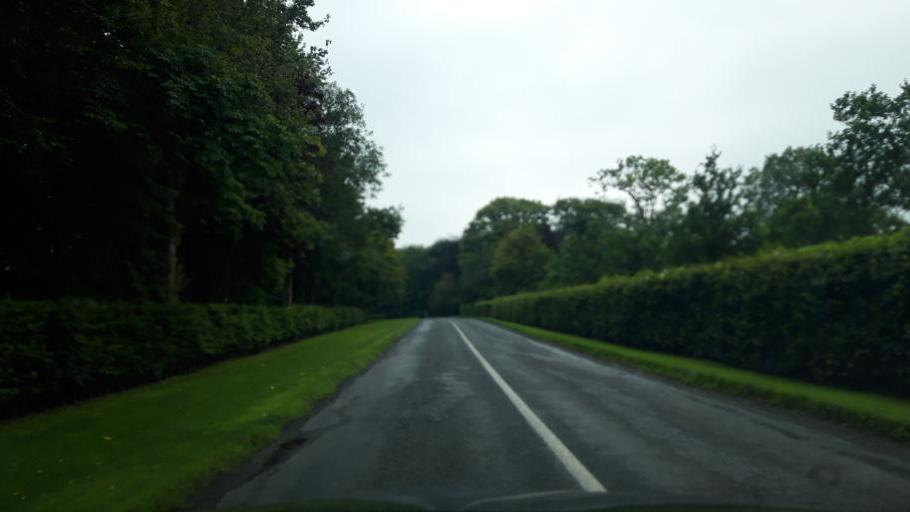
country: IE
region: Munster
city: Fethard
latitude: 52.5082
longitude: -7.6858
